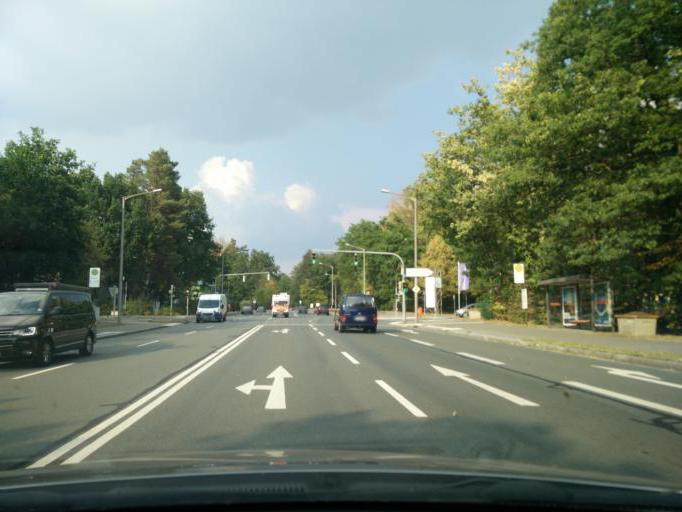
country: DE
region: Bavaria
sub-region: Regierungsbezirk Mittelfranken
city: Wendelstein
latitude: 49.4145
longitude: 11.1471
